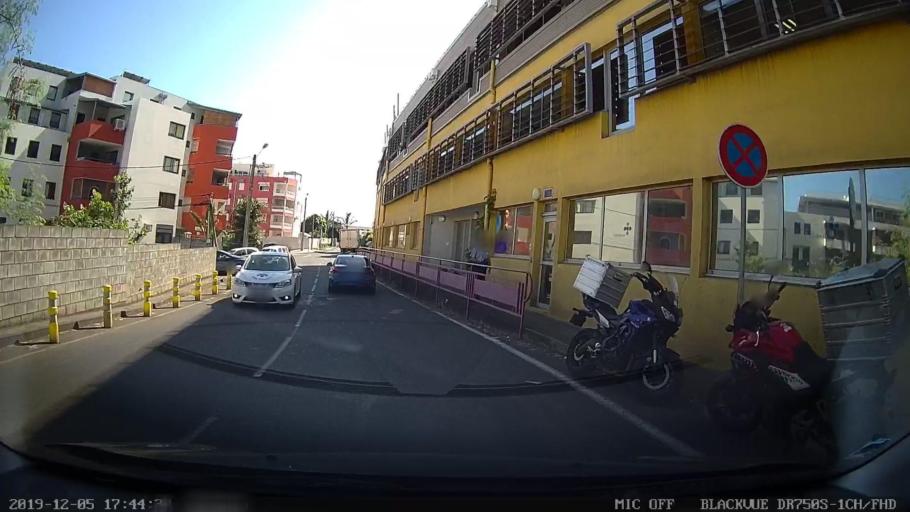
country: RE
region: Reunion
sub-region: Reunion
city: Saint-Denis
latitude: -20.9019
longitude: 55.4782
